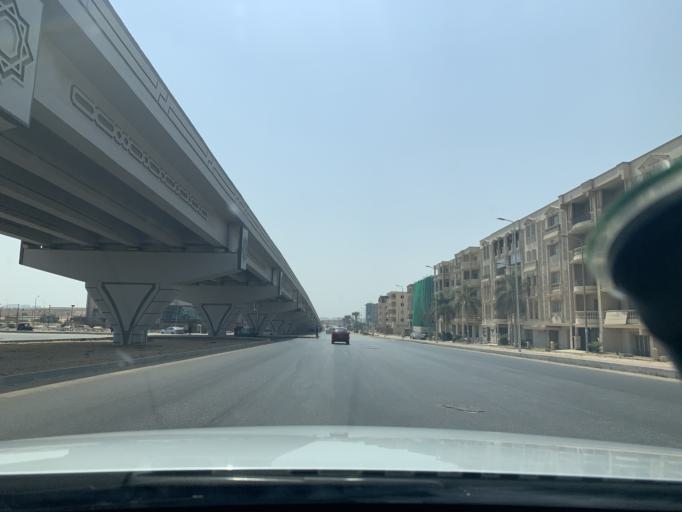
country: EG
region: Muhafazat al Qalyubiyah
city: Al Khankah
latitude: 30.0915
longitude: 31.3771
